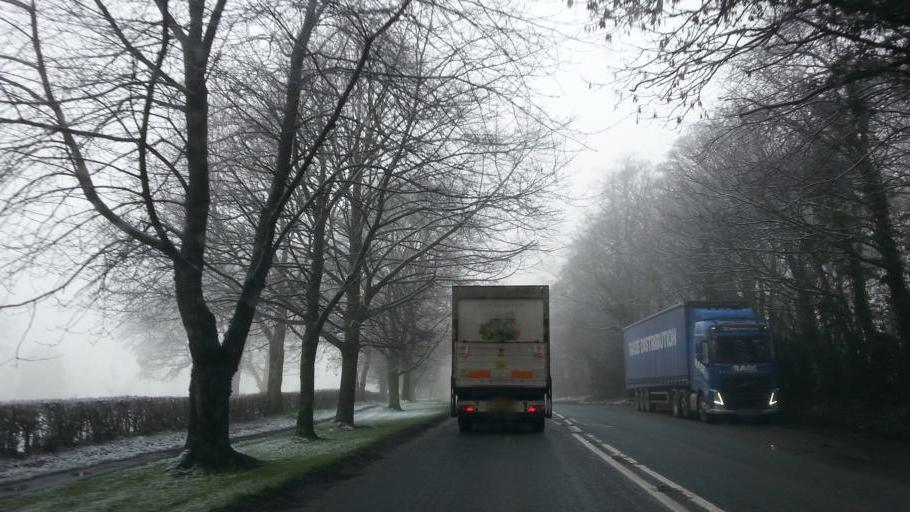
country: GB
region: England
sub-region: Cheshire East
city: Eaton
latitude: 53.1834
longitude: -2.2111
